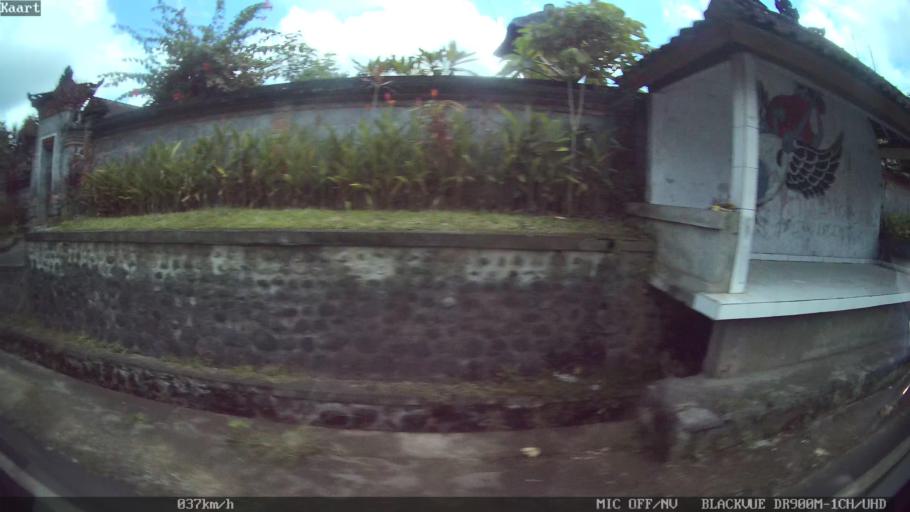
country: ID
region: Bali
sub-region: Kabupaten Gianyar
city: Ubud
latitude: -8.5412
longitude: 115.2804
